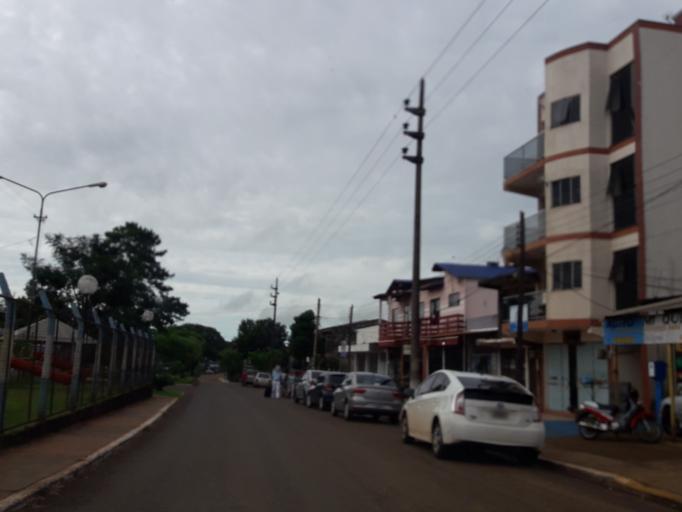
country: AR
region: Misiones
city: Bernardo de Irigoyen
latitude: -26.2572
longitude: -53.6475
